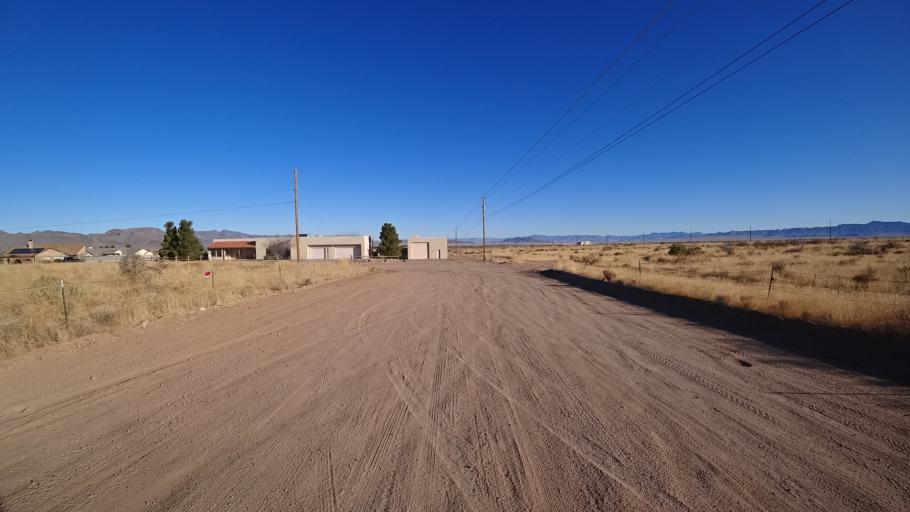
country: US
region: Arizona
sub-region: Mohave County
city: Kingman
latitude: 35.2027
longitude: -113.9939
